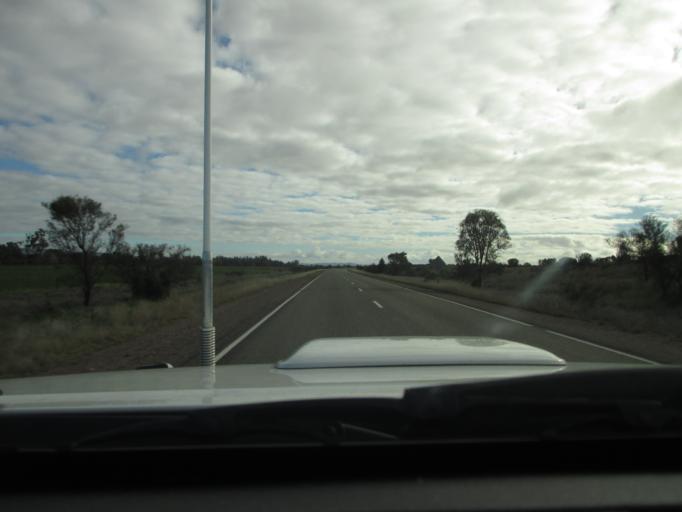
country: AU
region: South Australia
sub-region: Flinders Ranges
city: Quorn
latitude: -32.4753
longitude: 138.5411
